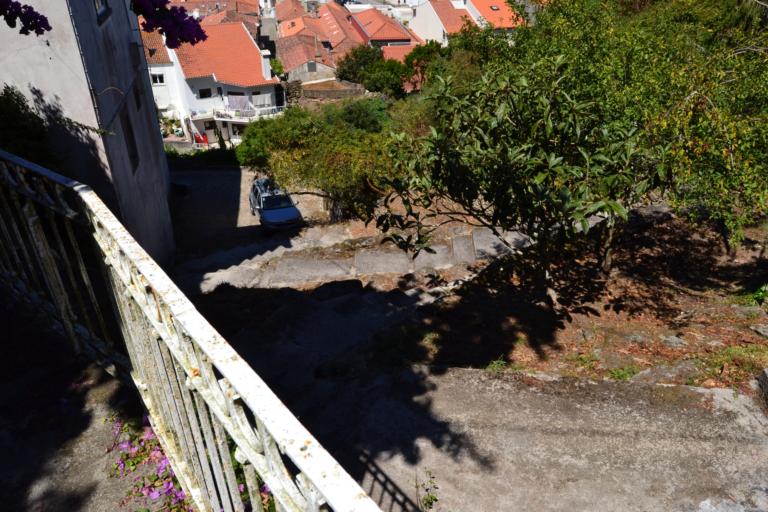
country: ES
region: Galicia
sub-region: Provincia de Pontevedra
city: A Guarda
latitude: 41.8704
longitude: -8.8417
